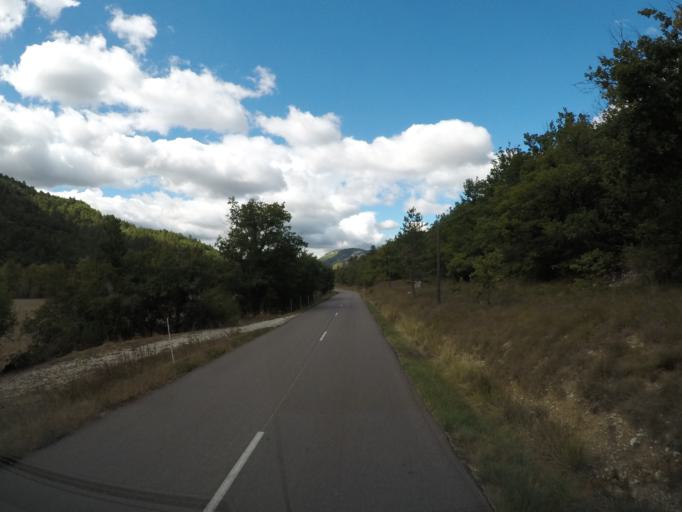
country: FR
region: Provence-Alpes-Cote d'Azur
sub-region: Departement du Vaucluse
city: Sault
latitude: 44.1780
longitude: 5.3999
